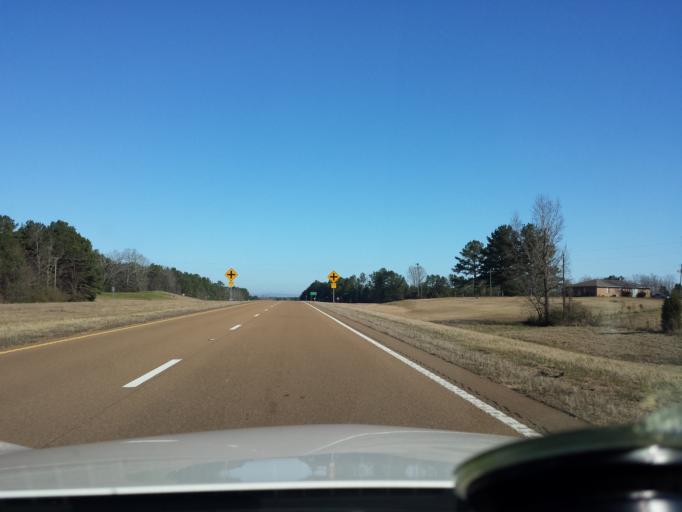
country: US
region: Mississippi
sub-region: Leake County
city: Carthage
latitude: 32.6191
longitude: -89.6914
